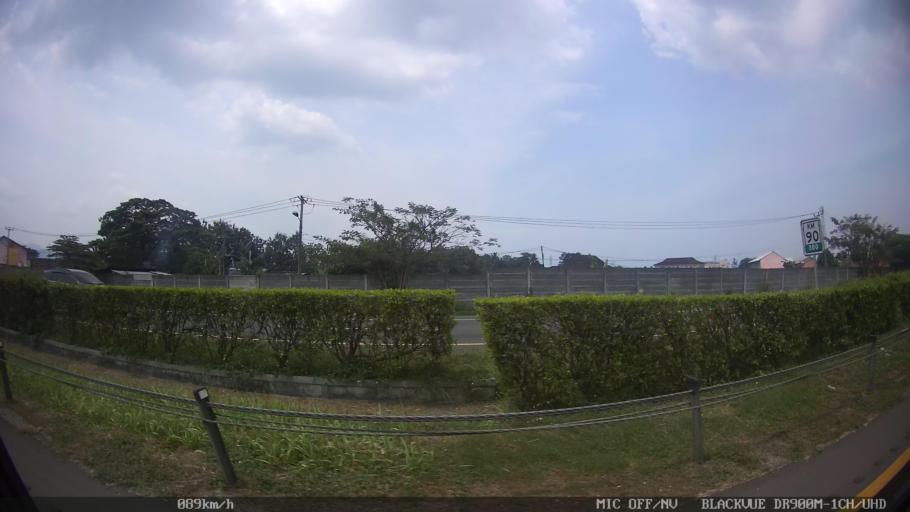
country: ID
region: Banten
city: Bojonegara
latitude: -6.0030
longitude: 106.0635
